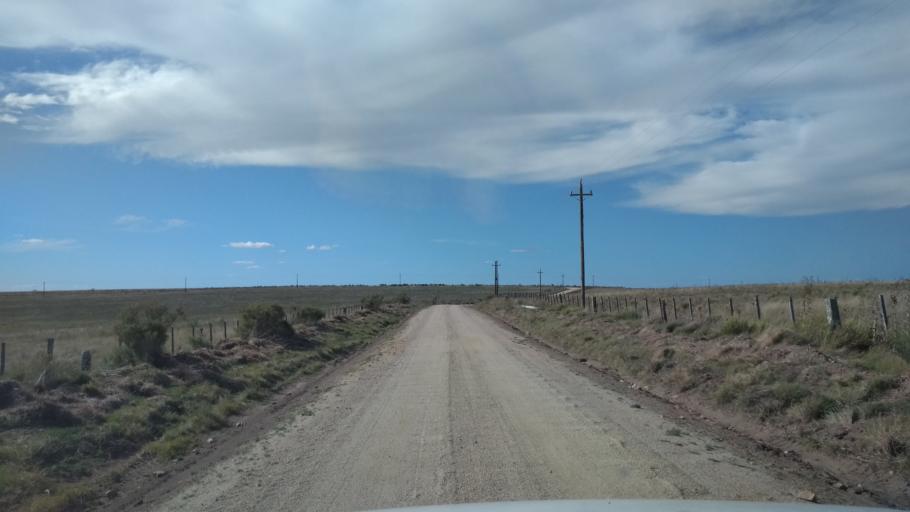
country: UY
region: Florida
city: Casupa
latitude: -34.0050
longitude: -55.7876
